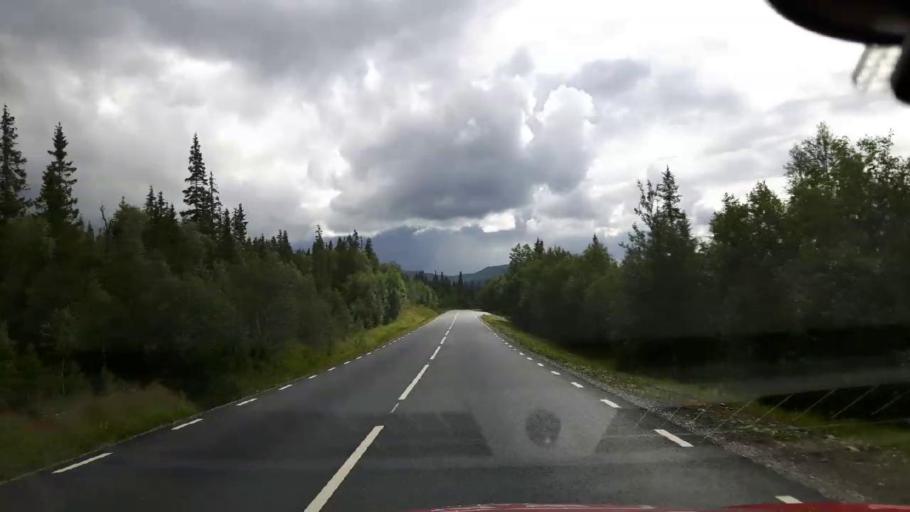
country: NO
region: Nord-Trondelag
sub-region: Royrvik
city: Royrvik
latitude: 64.8809
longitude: 14.2103
